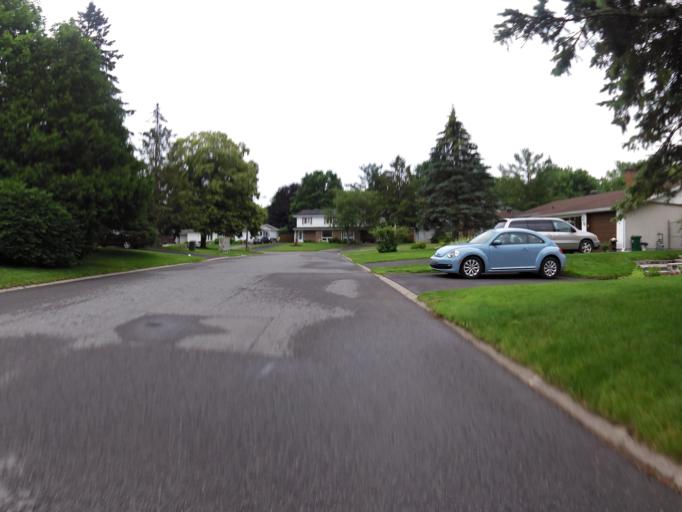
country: CA
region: Ontario
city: Bells Corners
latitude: 45.3359
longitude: -75.7763
